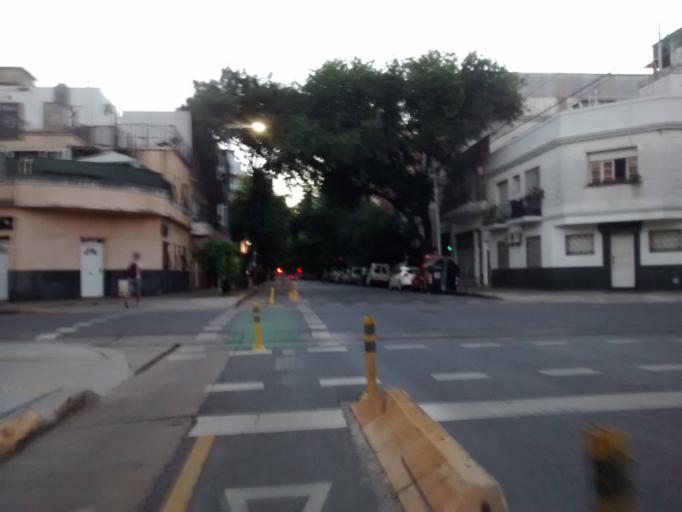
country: AR
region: Buenos Aires F.D.
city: Villa Santa Rita
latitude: -34.6041
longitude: -58.4514
